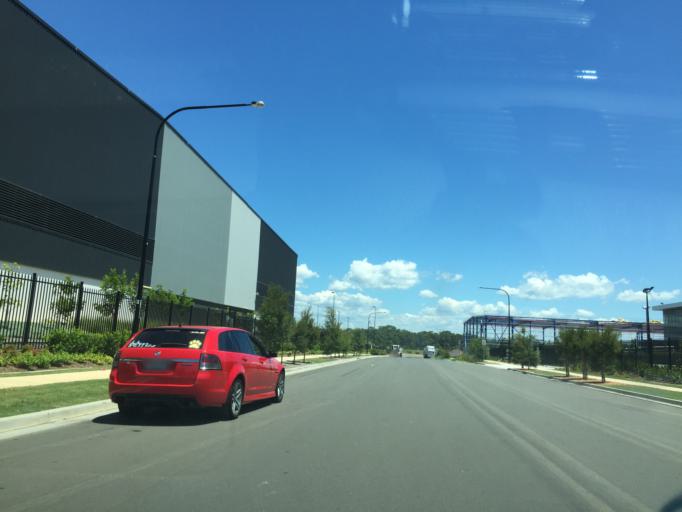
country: AU
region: New South Wales
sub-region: Blacktown
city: Doonside
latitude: -33.7937
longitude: 150.8681
